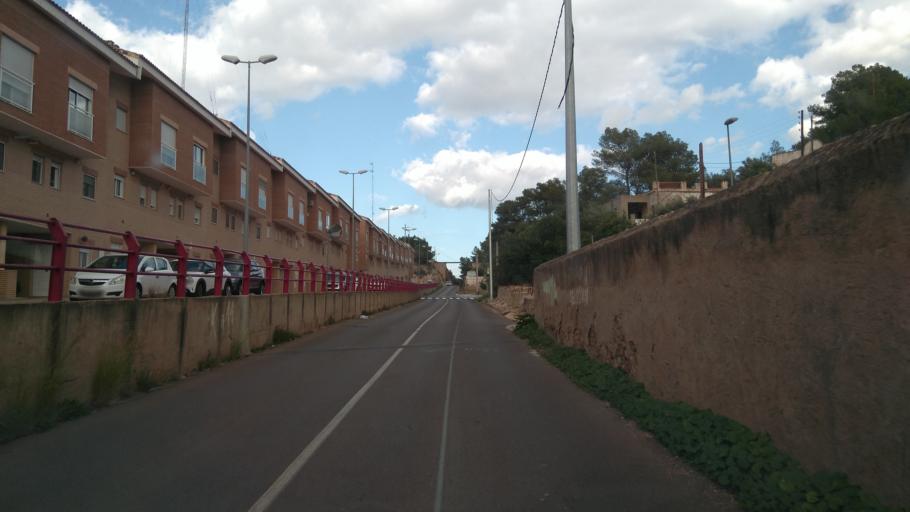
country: ES
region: Valencia
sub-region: Provincia de Valencia
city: Alzira
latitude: 39.1525
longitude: -0.4156
